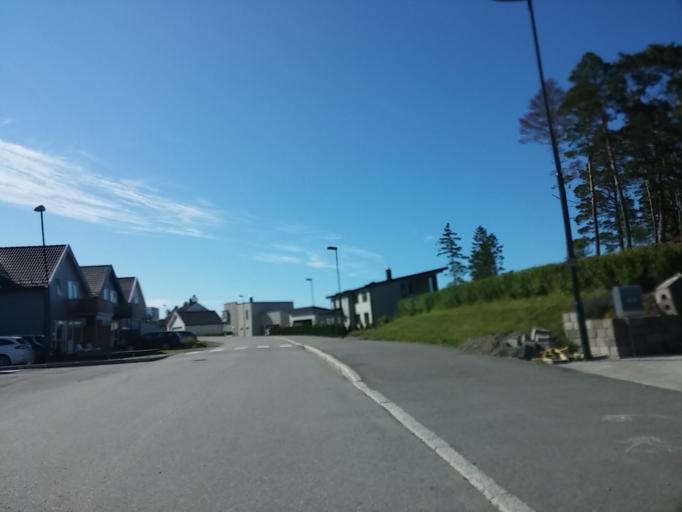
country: NO
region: Sor-Trondelag
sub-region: Malvik
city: Hommelvik
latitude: 63.4292
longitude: 10.7551
